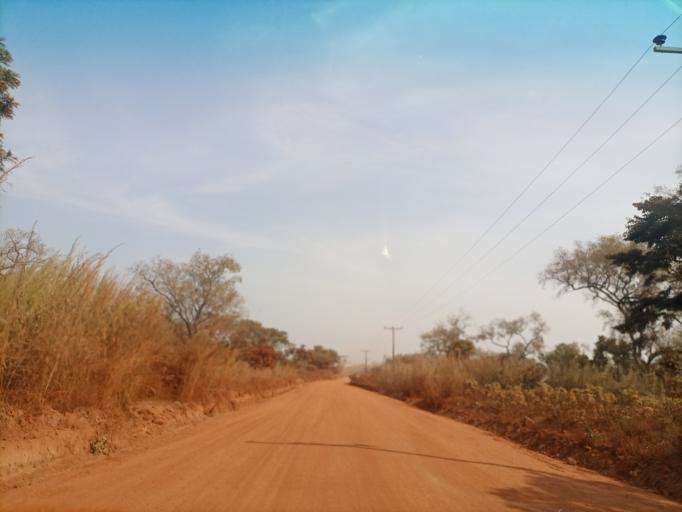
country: NG
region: Enugu
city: Eha Amufu
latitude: 6.6730
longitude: 7.7343
